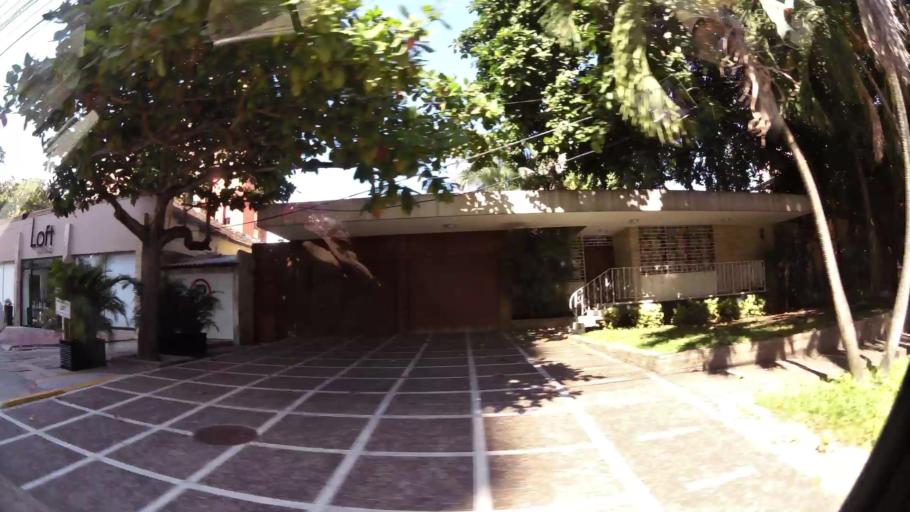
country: CO
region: Atlantico
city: Barranquilla
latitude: 11.0029
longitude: -74.8100
